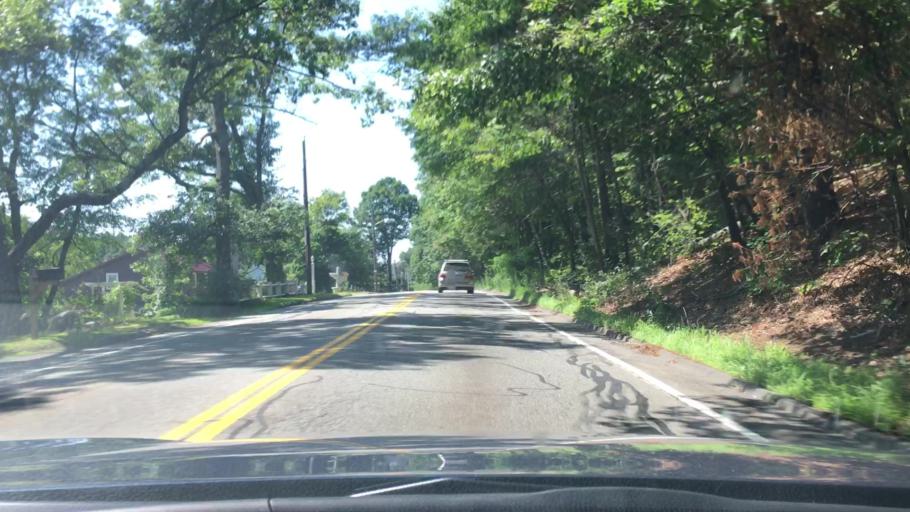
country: US
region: Massachusetts
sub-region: Middlesex County
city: Billerica
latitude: 42.5683
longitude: -71.2971
